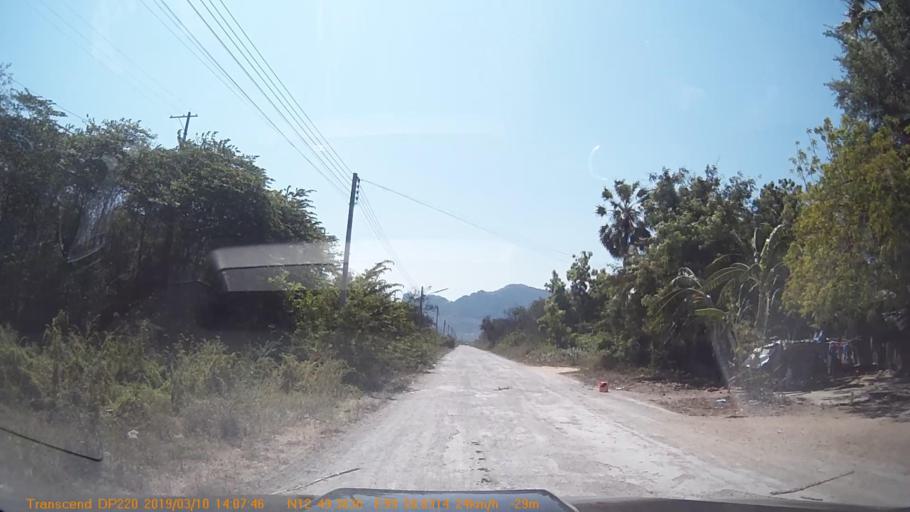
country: TH
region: Phetchaburi
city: Cha-am
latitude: 12.8227
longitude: 99.9805
